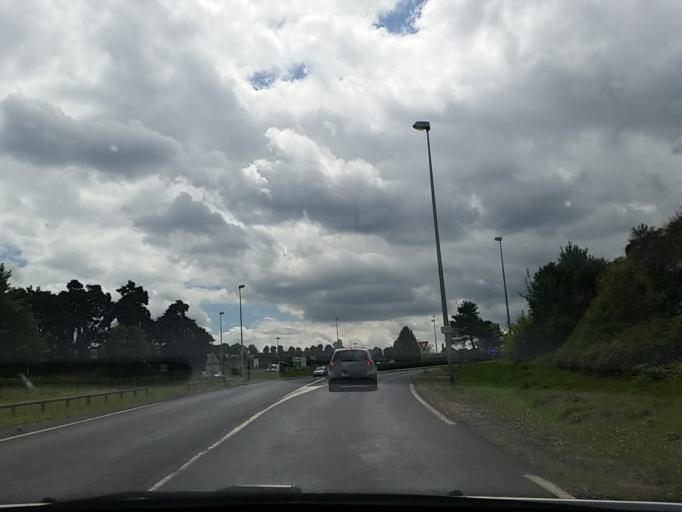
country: FR
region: Auvergne
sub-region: Departement du Cantal
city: Saint-Flour
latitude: 45.0284
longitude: 3.0656
